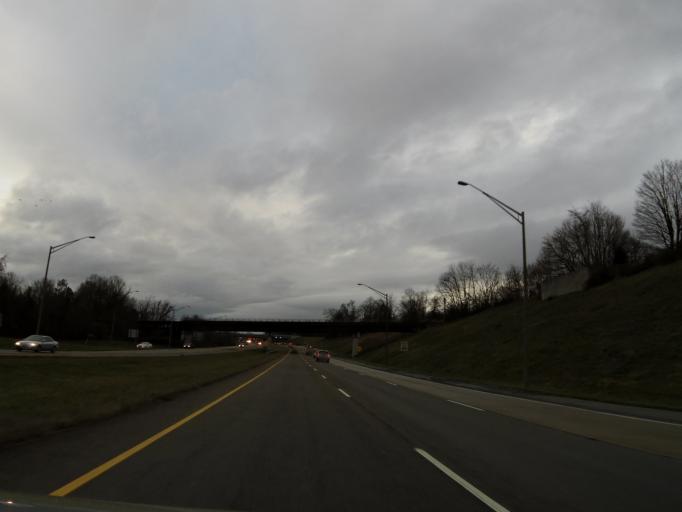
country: US
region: Tennessee
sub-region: Carter County
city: Pine Crest
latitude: 36.3103
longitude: -82.3330
